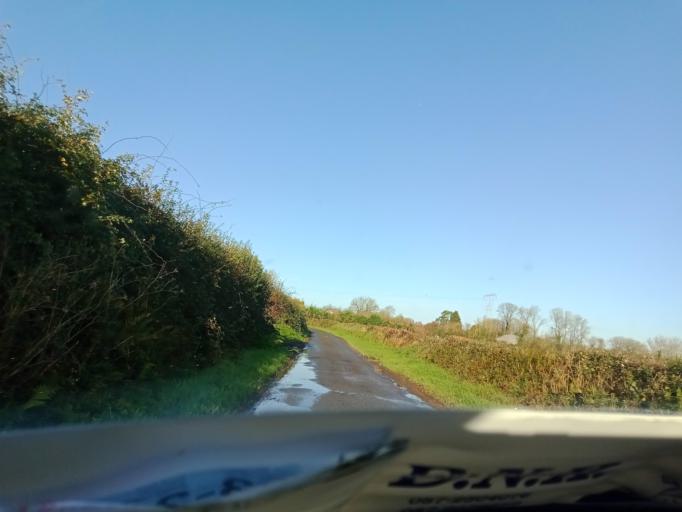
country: IE
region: Munster
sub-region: Waterford
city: Waterford
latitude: 52.2890
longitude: -7.1721
